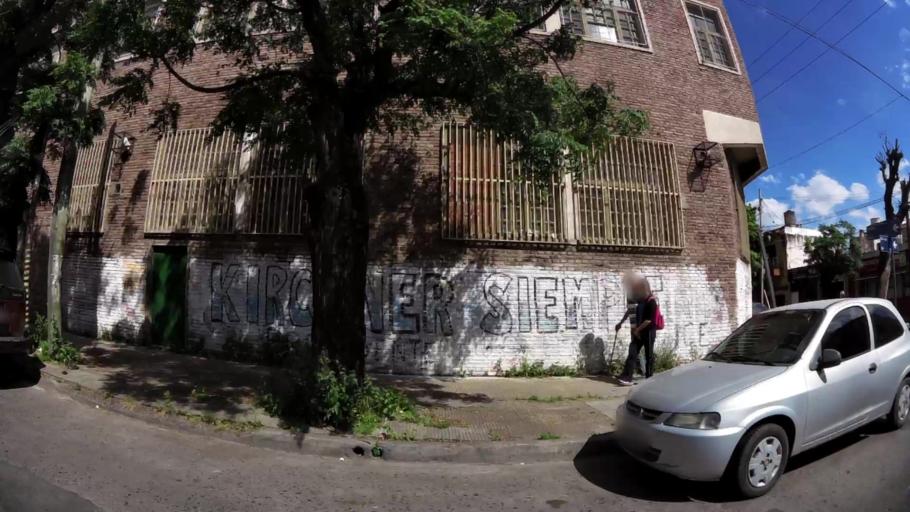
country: AR
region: Buenos Aires
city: San Justo
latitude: -34.6482
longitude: -58.5468
